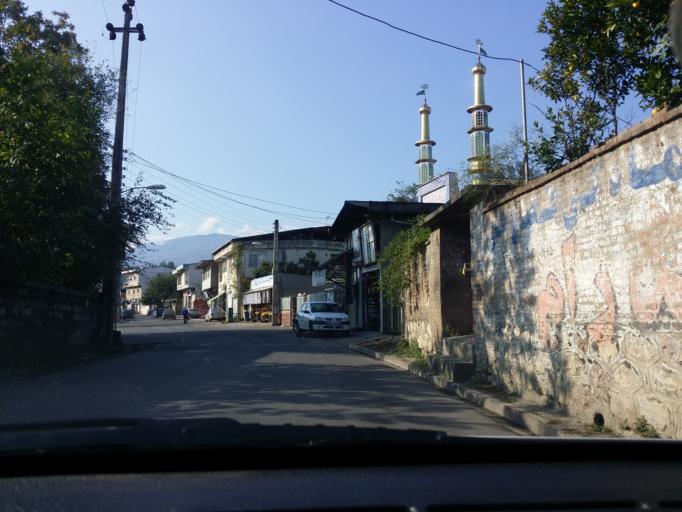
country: IR
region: Mazandaran
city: Chalus
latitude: 36.6523
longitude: 51.4135
